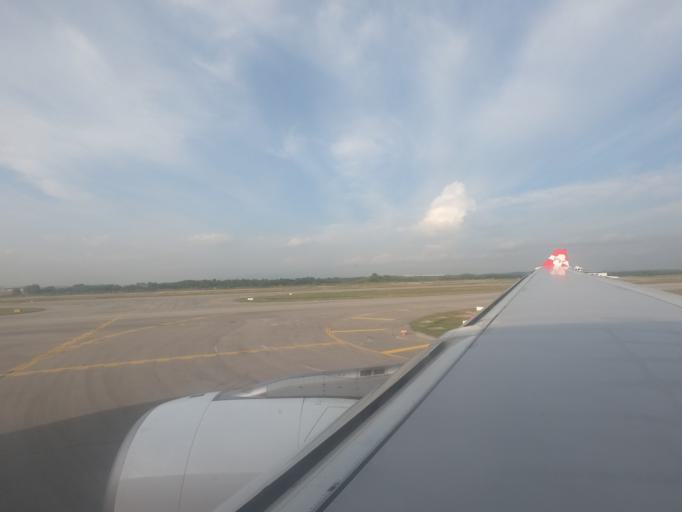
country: MY
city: Sungai Pelek New Village
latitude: 2.7270
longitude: 101.6862
